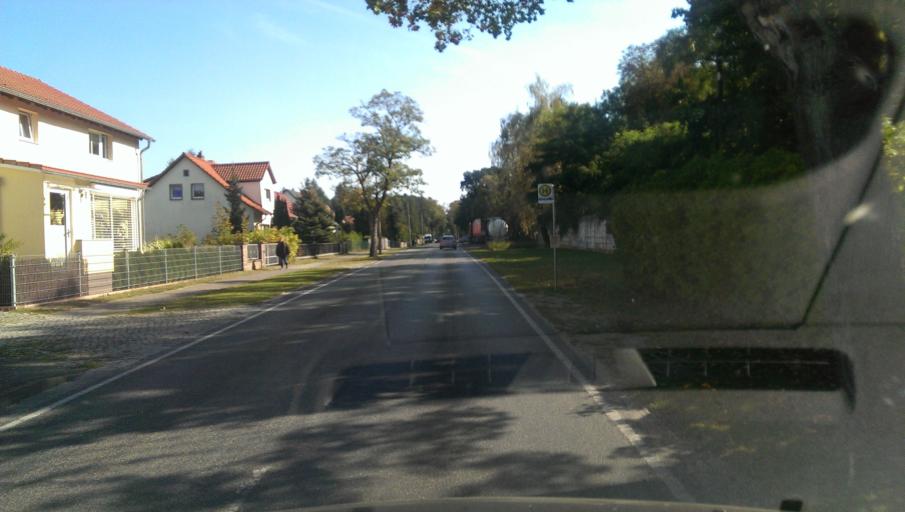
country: DE
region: Brandenburg
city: Teupitz
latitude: 52.1315
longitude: 13.6212
